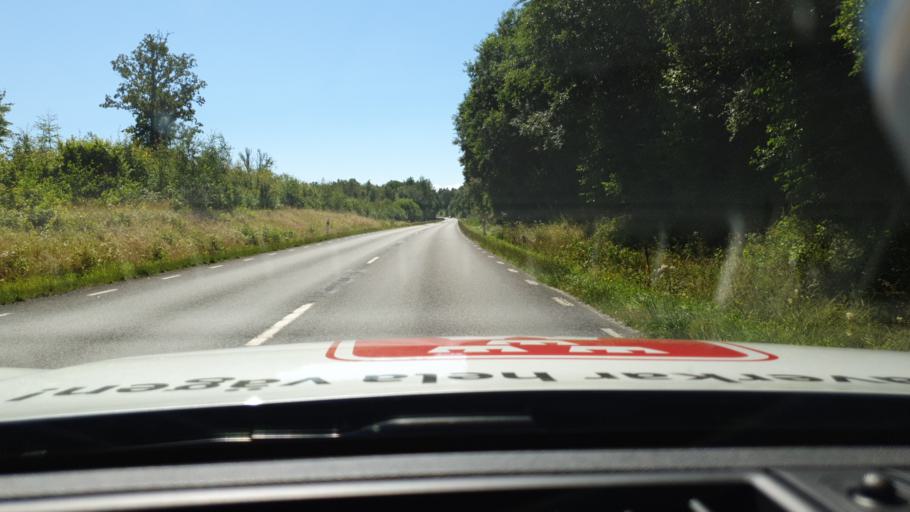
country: SE
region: Vaestra Goetaland
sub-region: Hjo Kommun
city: Hjo
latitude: 58.1208
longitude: 14.2159
